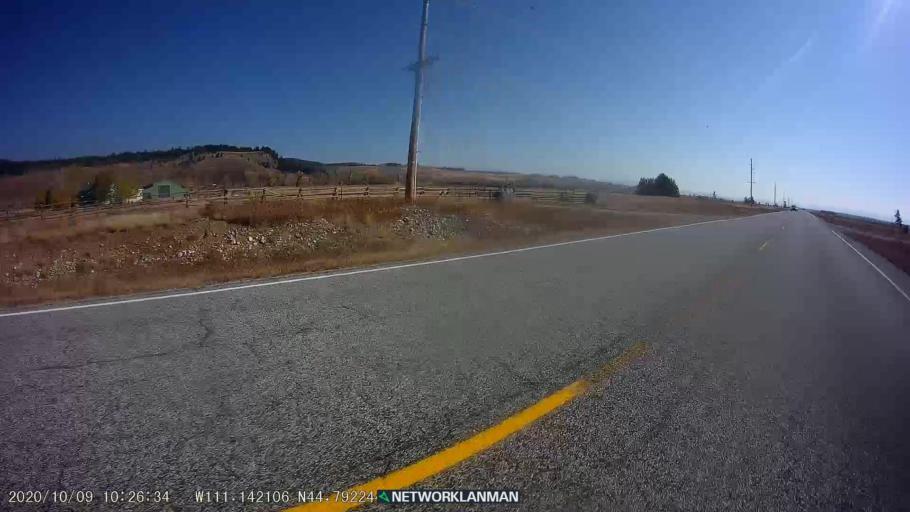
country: US
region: Montana
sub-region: Gallatin County
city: West Yellowstone
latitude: 44.7920
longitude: -111.1420
